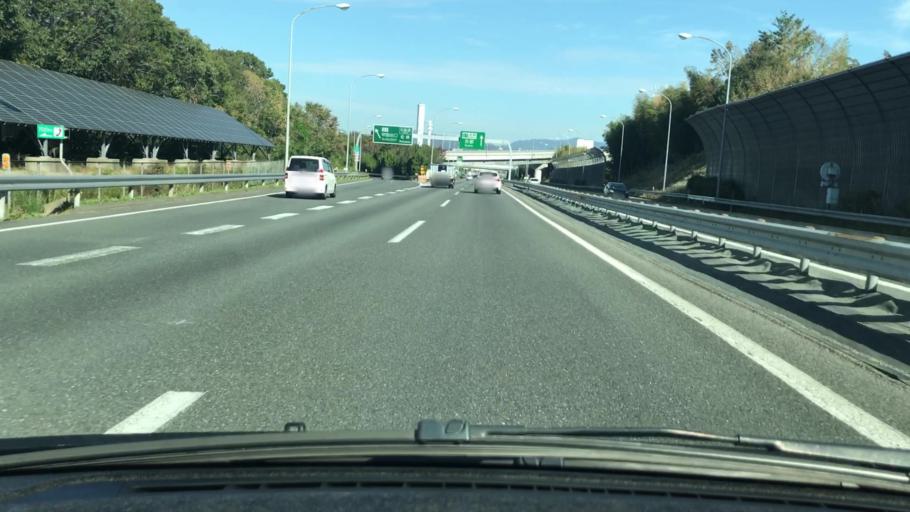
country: JP
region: Osaka
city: Ibaraki
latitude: 34.8002
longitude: 135.5400
